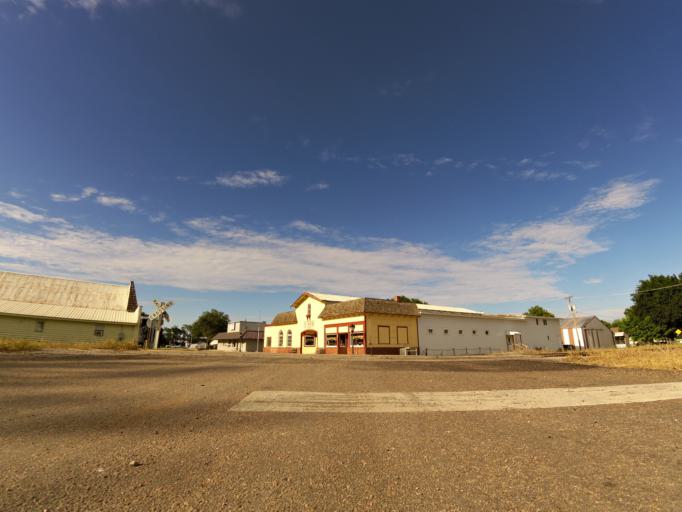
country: US
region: Kansas
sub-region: Reno County
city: Haven
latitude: 37.9399
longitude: -97.8698
